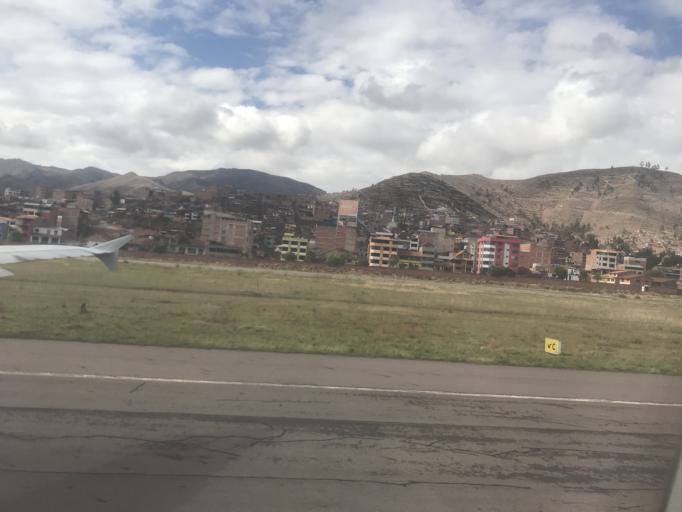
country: PE
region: Cusco
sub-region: Provincia de Cusco
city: Cusco
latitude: -13.5343
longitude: -71.9530
